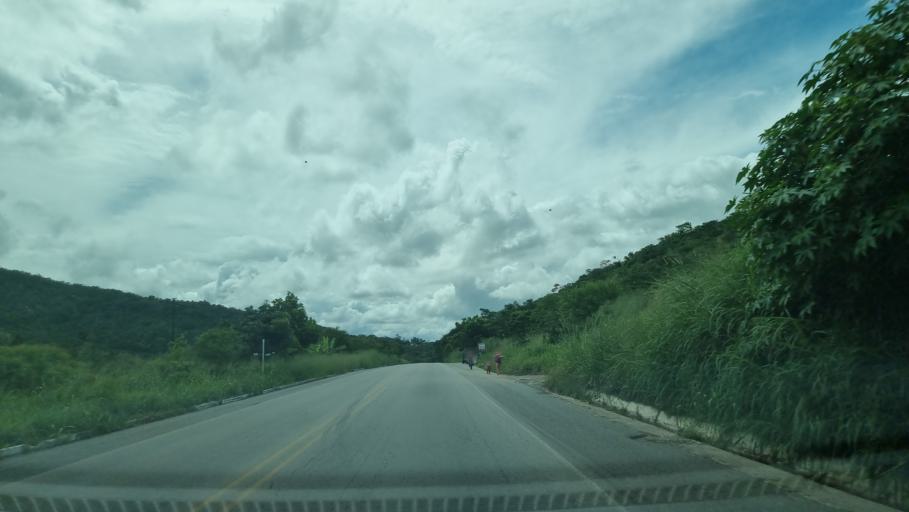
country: BR
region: Pernambuco
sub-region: Caruaru
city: Caruaru
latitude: -8.3624
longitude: -35.9863
